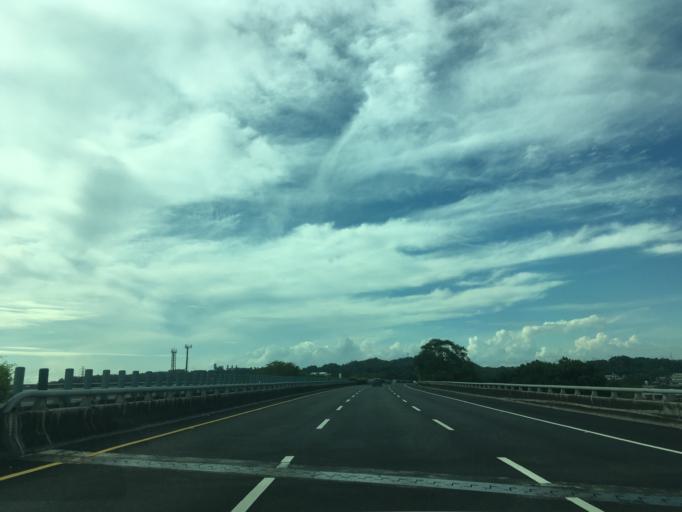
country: TW
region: Taiwan
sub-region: Chiayi
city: Jiayi Shi
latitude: 23.5130
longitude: 120.4856
